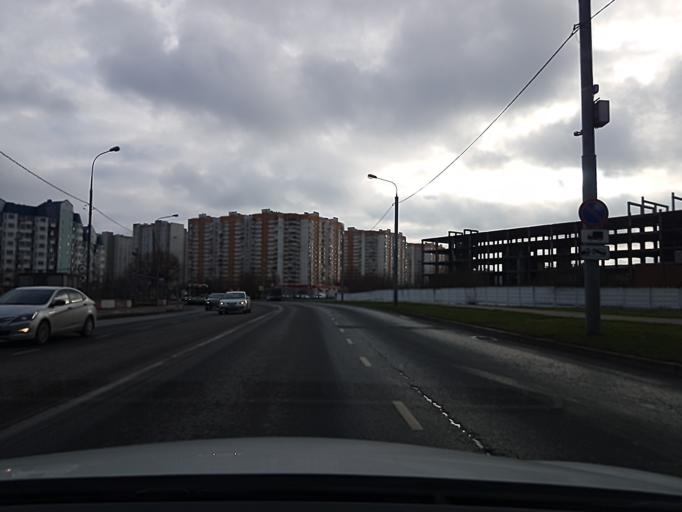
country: RU
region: Moskovskaya
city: Pavshino
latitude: 55.8393
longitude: 37.3511
